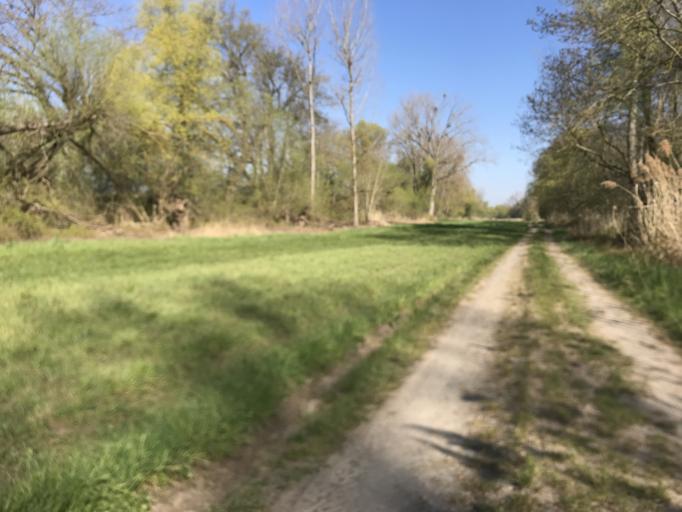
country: DE
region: Hesse
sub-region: Regierungsbezirk Darmstadt
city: Ginsheim-Gustavsburg
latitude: 49.9500
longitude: 8.3511
